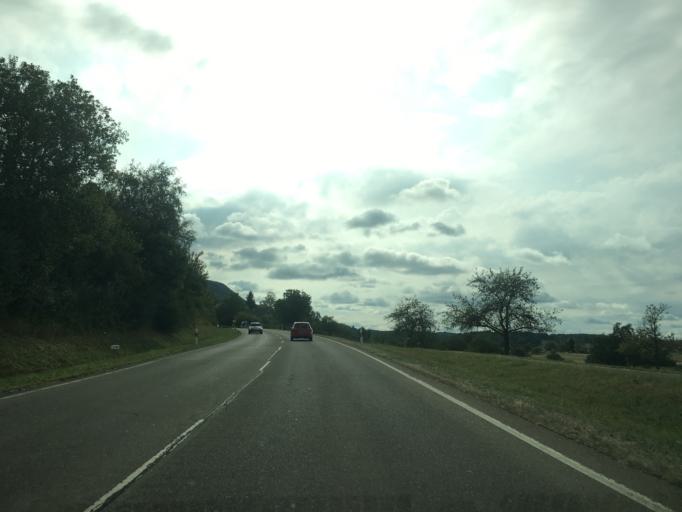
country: DE
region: Baden-Wuerttemberg
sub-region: Tuebingen Region
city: Gomaringen
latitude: 48.4439
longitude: 9.1509
